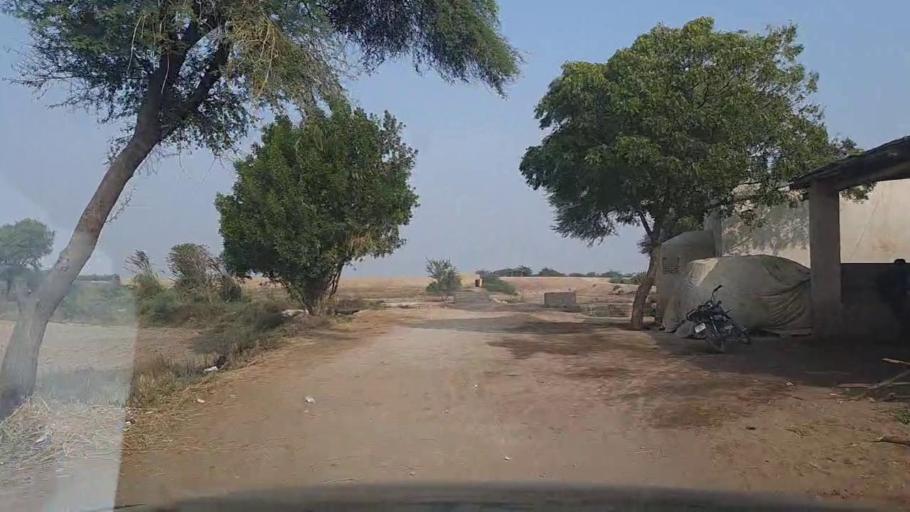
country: PK
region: Sindh
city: Bulri
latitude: 24.9419
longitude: 68.2811
